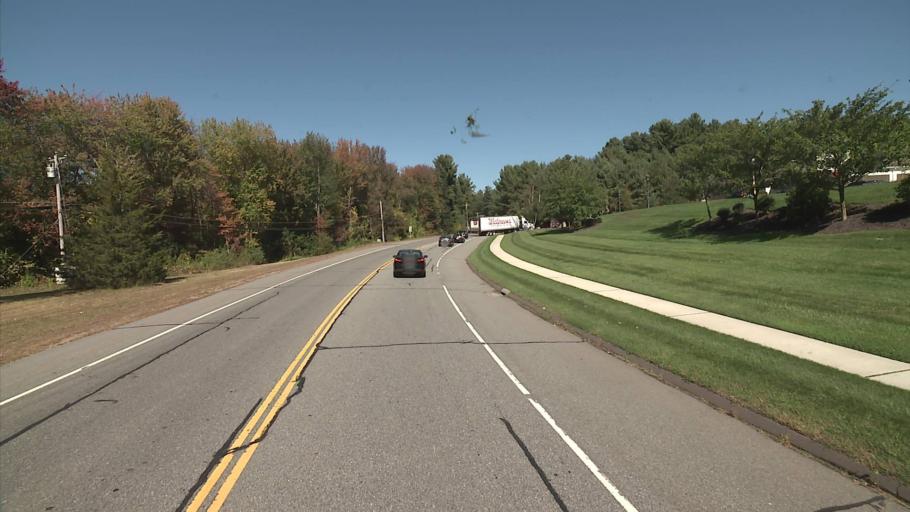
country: US
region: Connecticut
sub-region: Hartford County
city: Manchester
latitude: 41.7138
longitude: -72.5266
